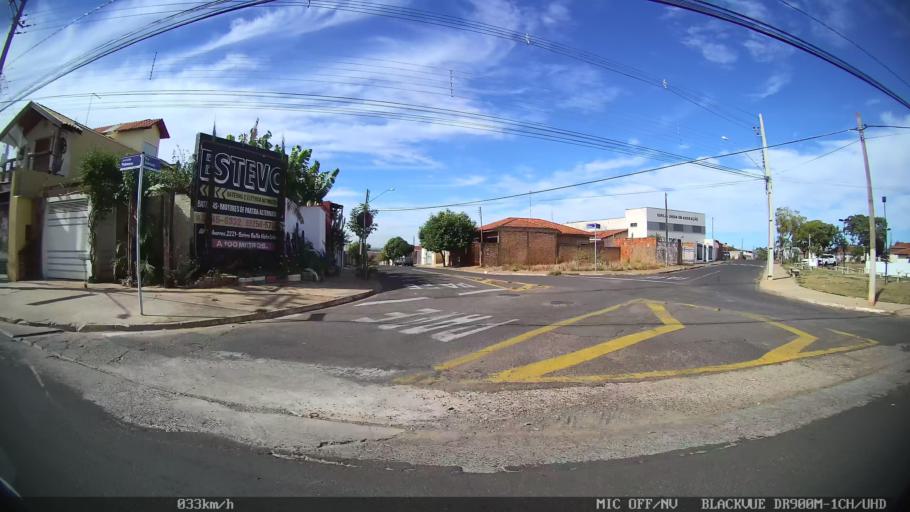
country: BR
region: Sao Paulo
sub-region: Catanduva
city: Catanduva
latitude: -21.1237
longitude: -48.9467
